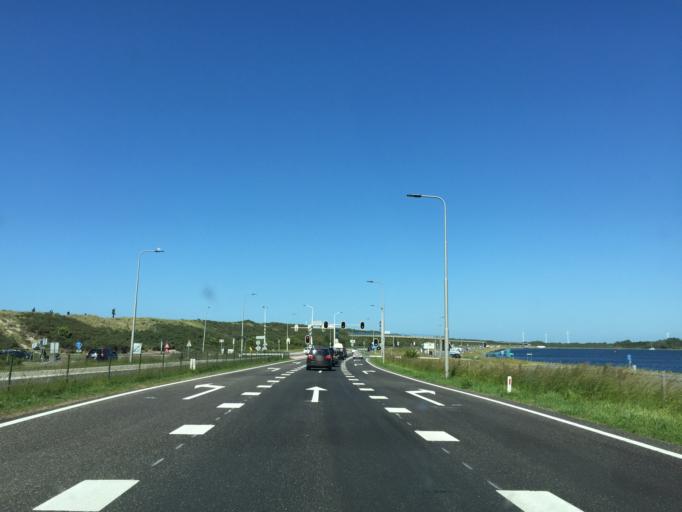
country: NL
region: Zeeland
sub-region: Gemeente Veere
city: Veere
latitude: 51.5845
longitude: 3.6271
